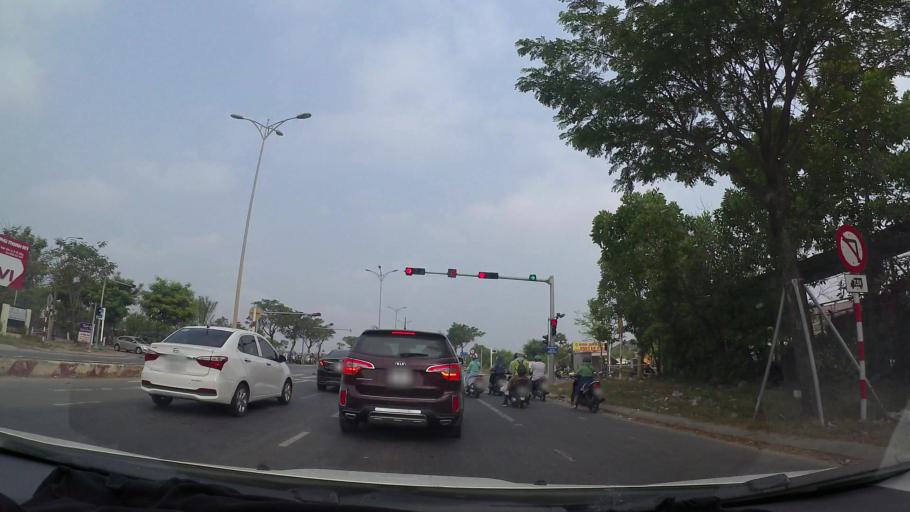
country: VN
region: Da Nang
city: Cam Le
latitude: 16.0108
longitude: 108.2174
